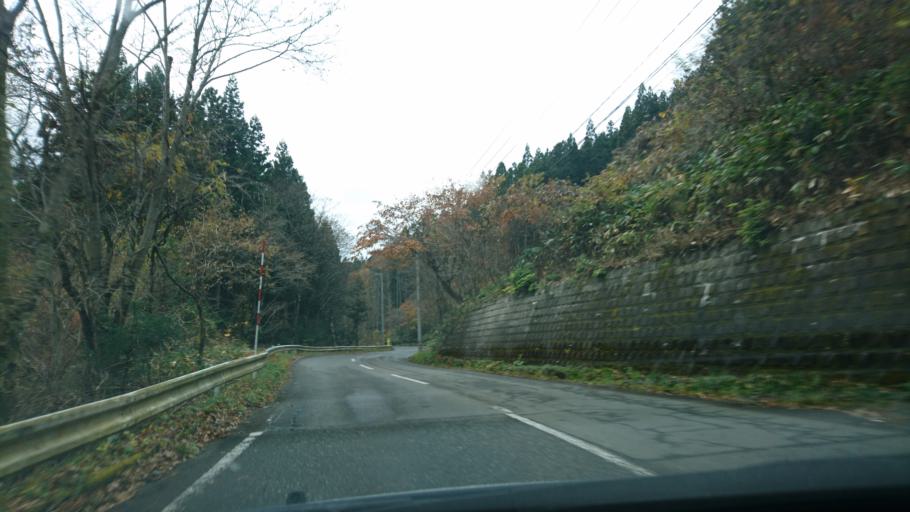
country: JP
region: Iwate
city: Ichinoseki
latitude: 38.9127
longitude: 140.8799
